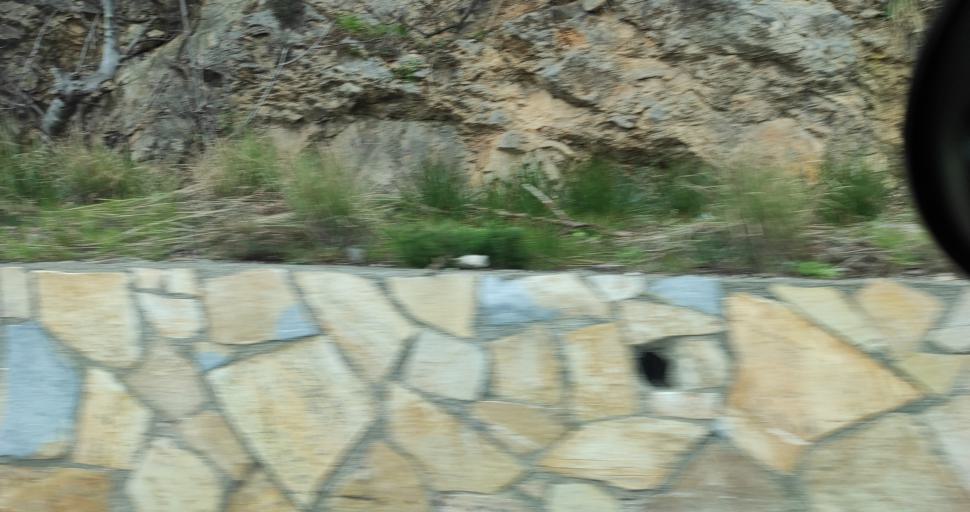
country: AL
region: Lezhe
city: Shengjin
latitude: 41.8054
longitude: 19.6117
